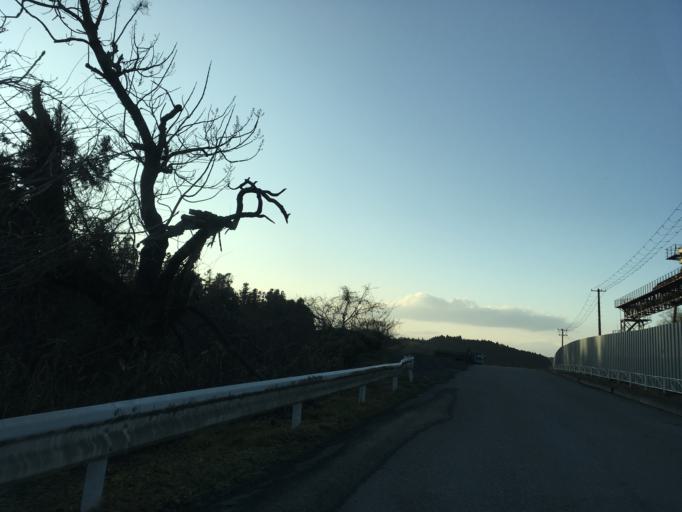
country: JP
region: Iwate
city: Ichinoseki
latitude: 38.8056
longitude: 141.2229
